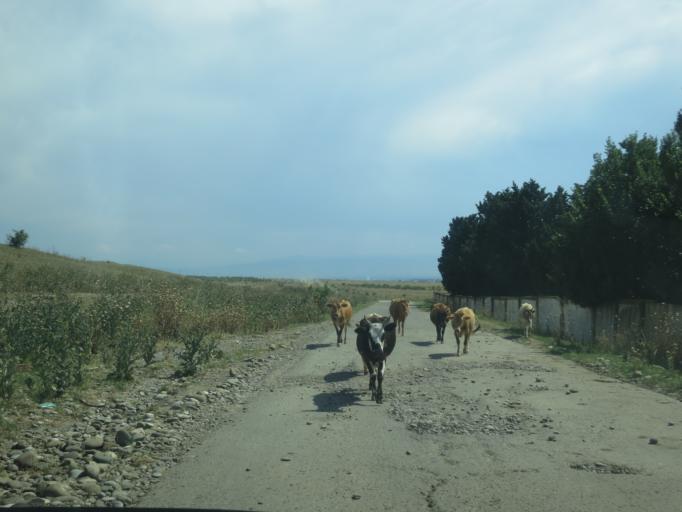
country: GE
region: Kvemo Kartli
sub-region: Gardabani
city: Gardabani
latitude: 41.4980
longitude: 45.1895
